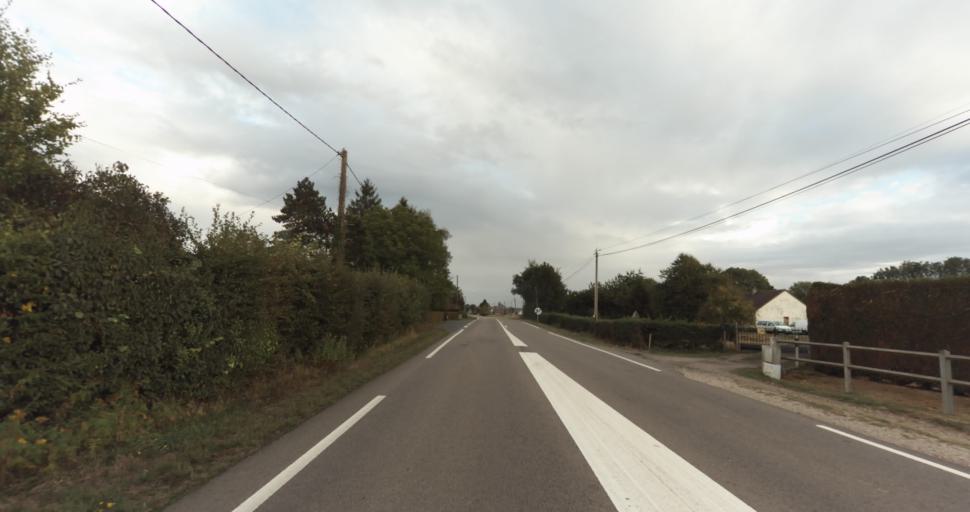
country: FR
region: Lower Normandy
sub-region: Departement de l'Orne
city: Vimoutiers
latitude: 48.9223
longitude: 0.2257
